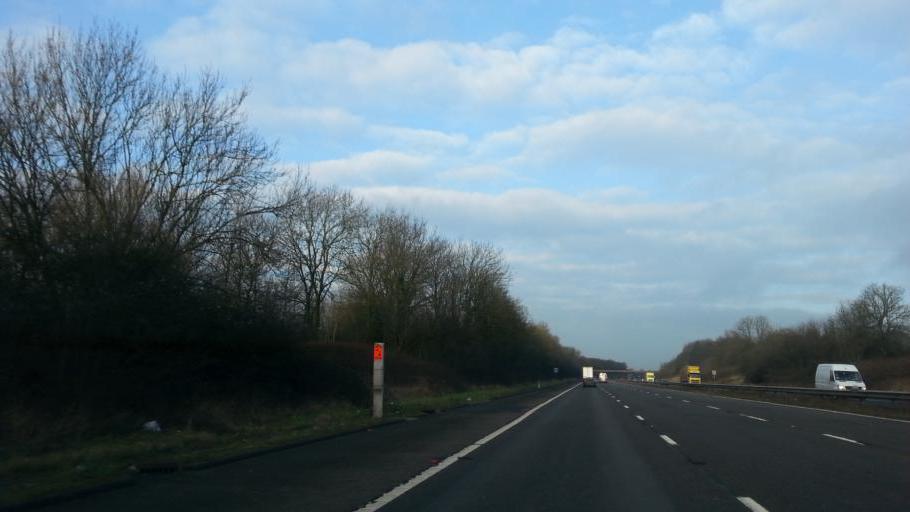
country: GB
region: England
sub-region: Gloucestershire
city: Dursley
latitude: 51.6980
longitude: -2.3927
